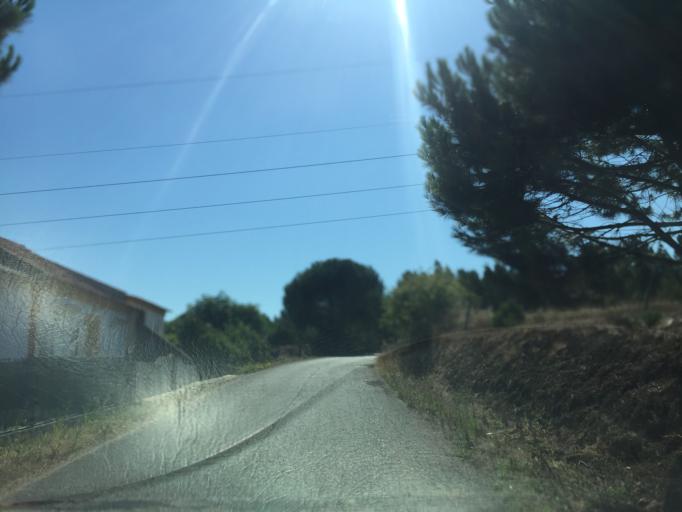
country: PT
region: Santarem
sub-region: Tomar
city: Tomar
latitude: 39.5710
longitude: -8.3224
